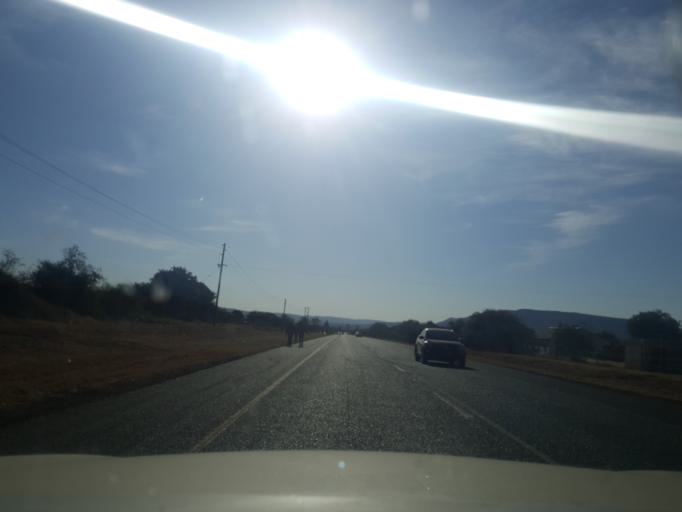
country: ZA
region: North-West
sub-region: Ngaka Modiri Molema District Municipality
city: Zeerust
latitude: -25.4647
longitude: 25.8876
